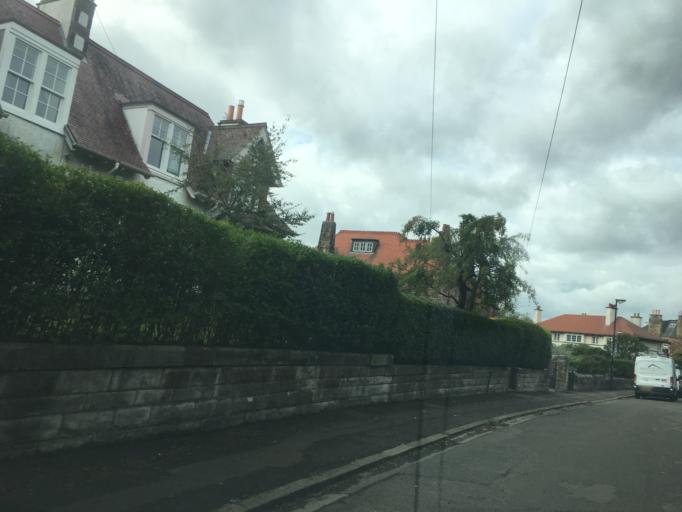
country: GB
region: Scotland
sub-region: Edinburgh
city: Edinburgh
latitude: 55.9198
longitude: -3.2061
